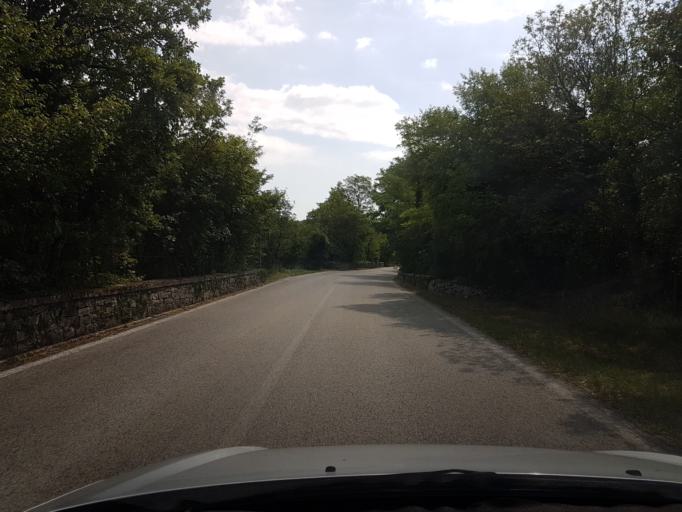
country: IT
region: Friuli Venezia Giulia
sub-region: Provincia di Trieste
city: Zolla
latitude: 45.7191
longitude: 13.7850
